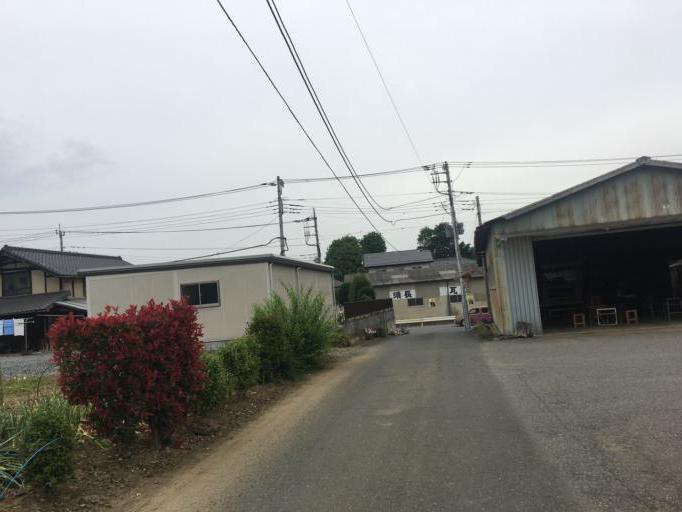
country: JP
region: Saitama
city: Sakado
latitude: 36.0172
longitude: 139.4373
